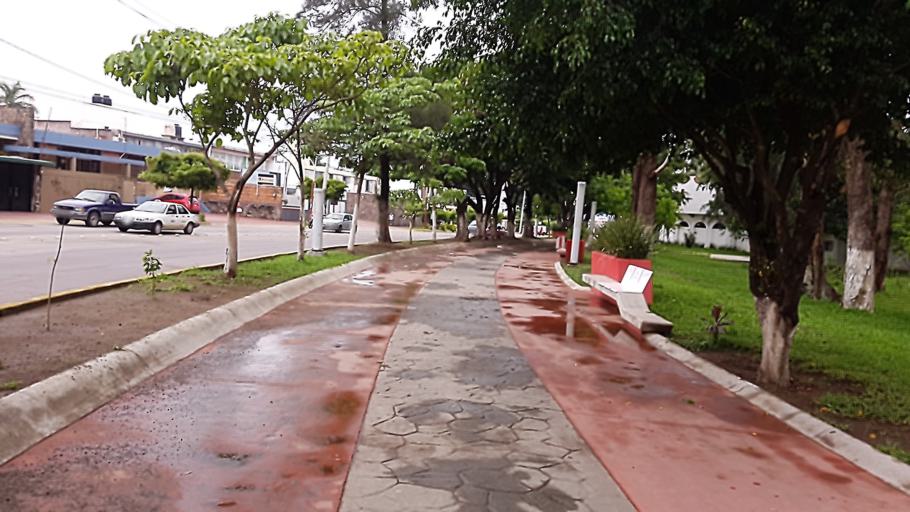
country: MX
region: Nayarit
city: Tepic
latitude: 21.5028
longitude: -104.9021
